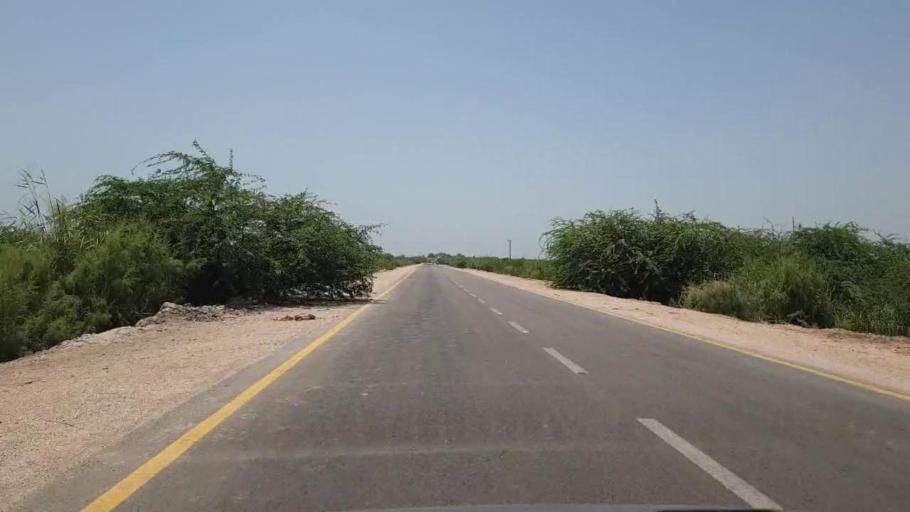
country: PK
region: Sindh
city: Sakrand
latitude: 26.1154
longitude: 68.3868
